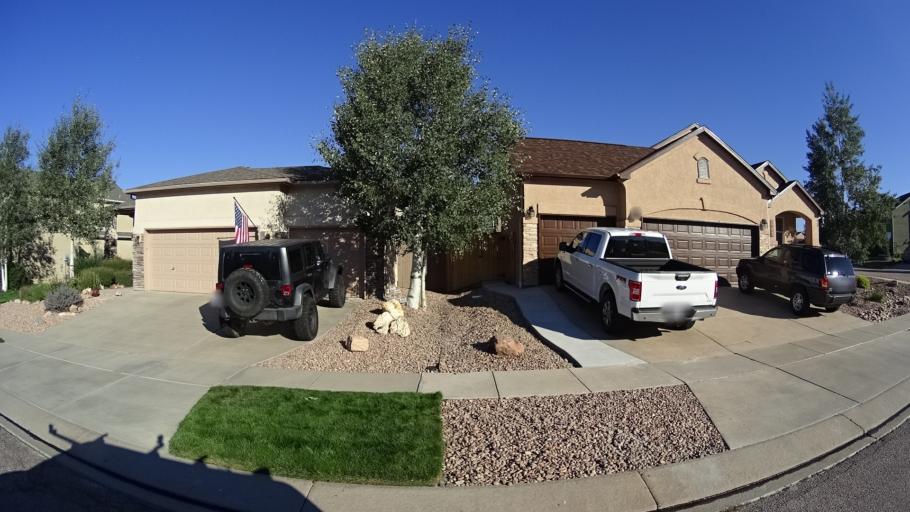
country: US
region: Colorado
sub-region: El Paso County
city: Black Forest
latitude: 38.9847
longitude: -104.7706
